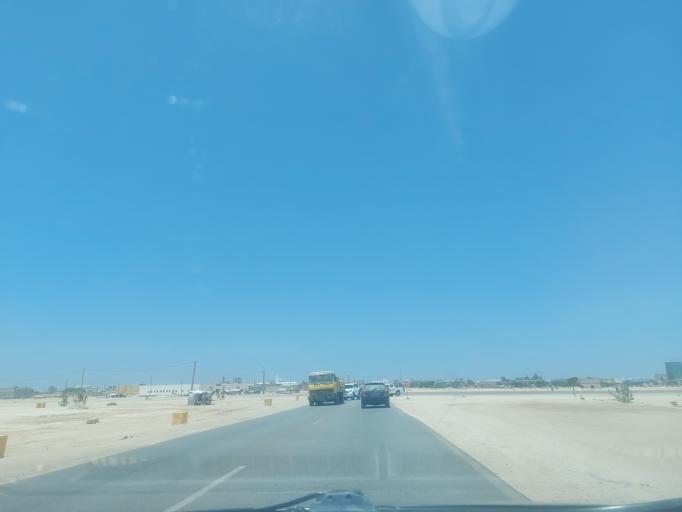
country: MR
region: Nouakchott
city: Nouakchott
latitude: 18.0872
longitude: -15.9555
